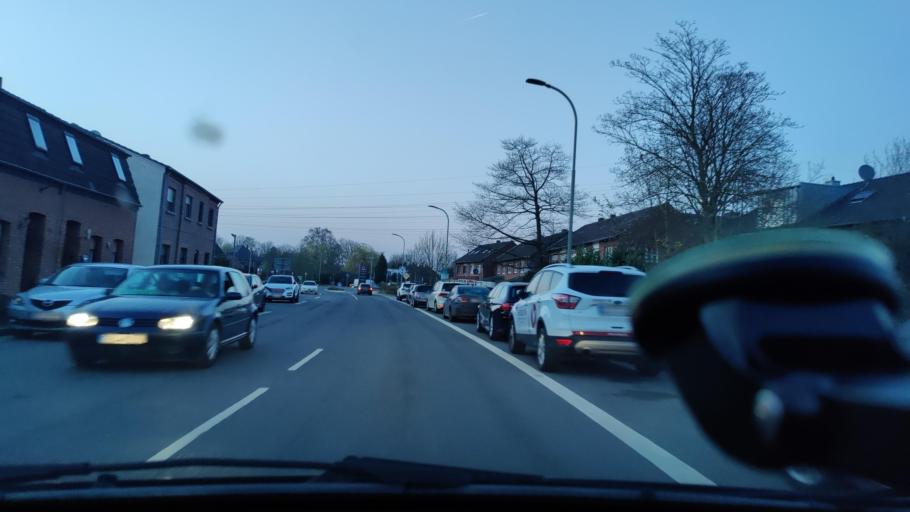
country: DE
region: North Rhine-Westphalia
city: Geldern
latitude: 51.5098
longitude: 6.3325
